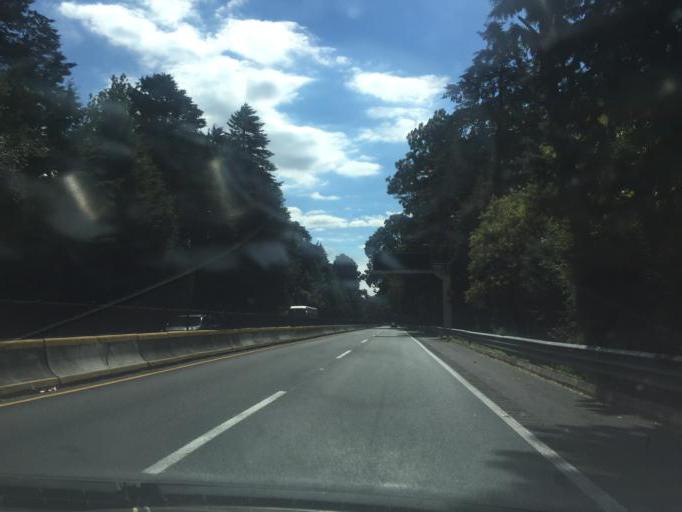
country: MX
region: Morelos
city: Tres Marias
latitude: 19.0429
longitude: -99.2332
